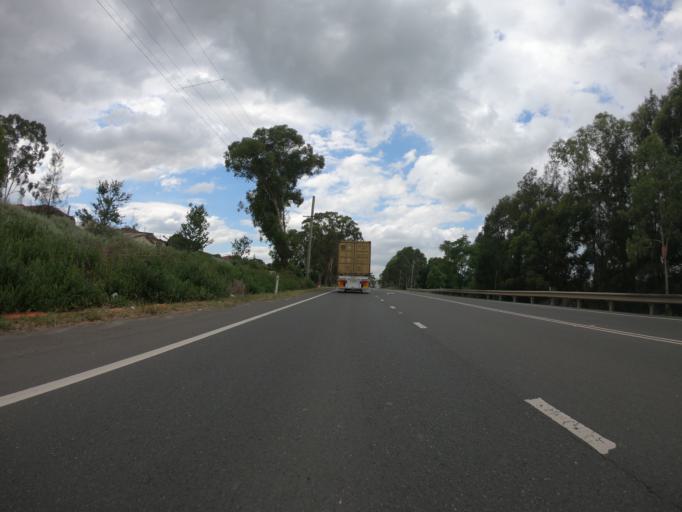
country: AU
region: New South Wales
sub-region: Blacktown
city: Mount Druitt
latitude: -33.8108
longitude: 150.7869
